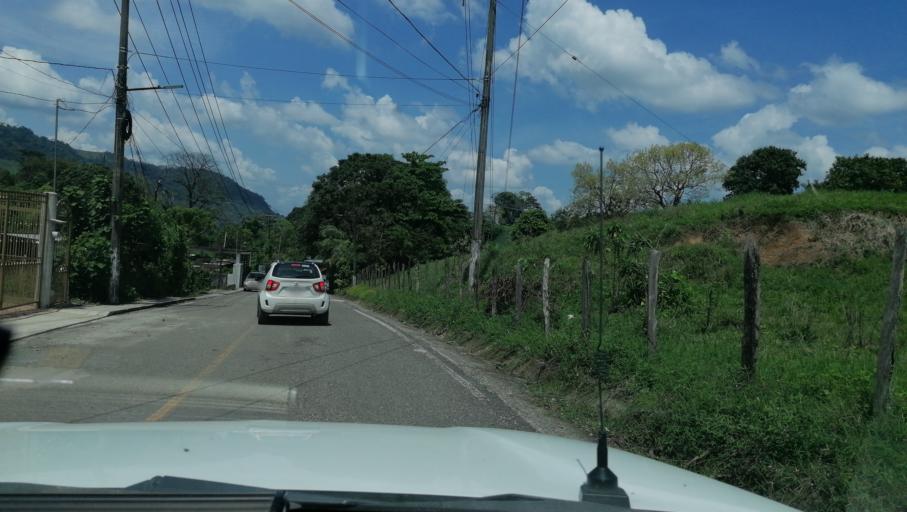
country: MX
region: Chiapas
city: Pichucalco
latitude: 17.5033
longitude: -93.1149
